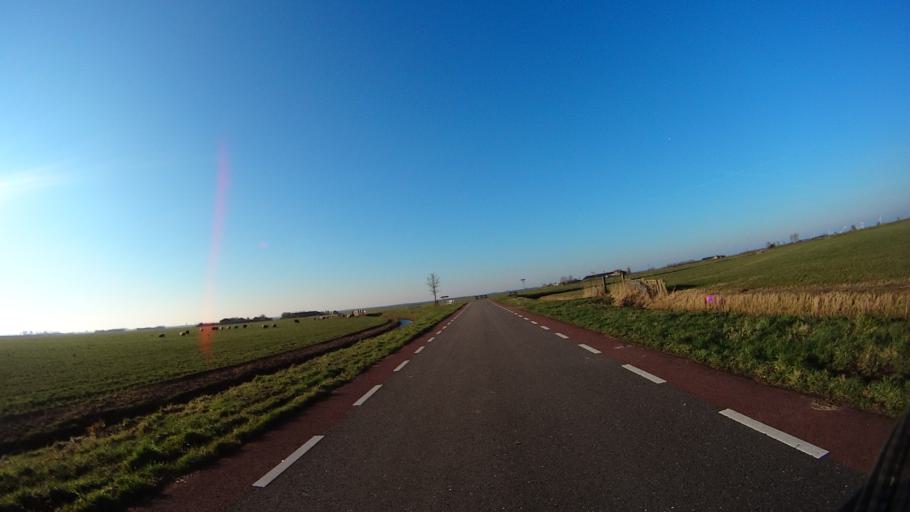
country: NL
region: Utrecht
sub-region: Gemeente Bunschoten
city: Spakenburg
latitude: 52.2560
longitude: 5.3255
